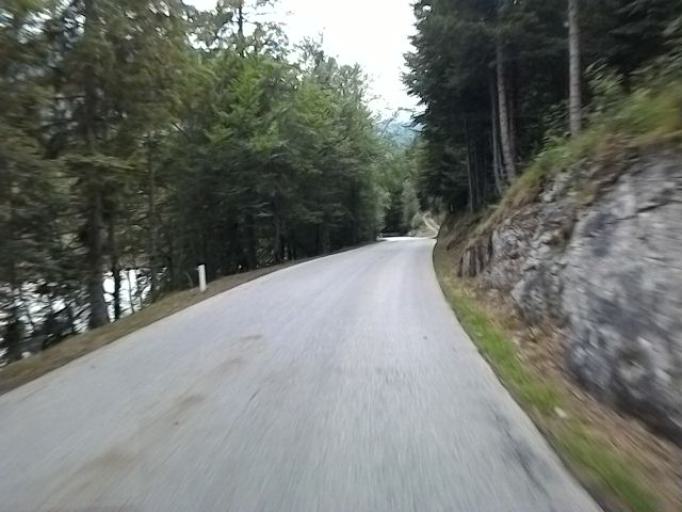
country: DE
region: Bavaria
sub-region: Upper Bavaria
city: Jachenau
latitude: 47.4684
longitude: 11.4798
